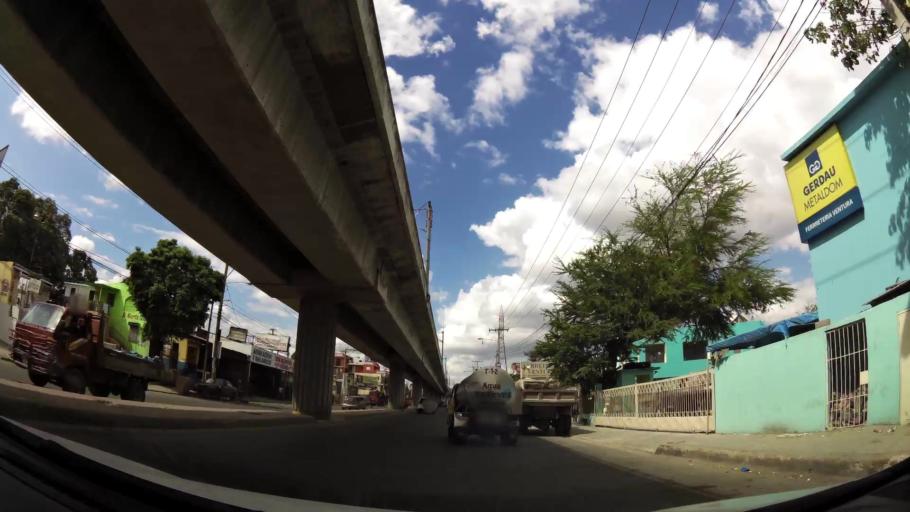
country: DO
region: Nacional
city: Ensanche Luperon
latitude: 18.5329
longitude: -69.9068
